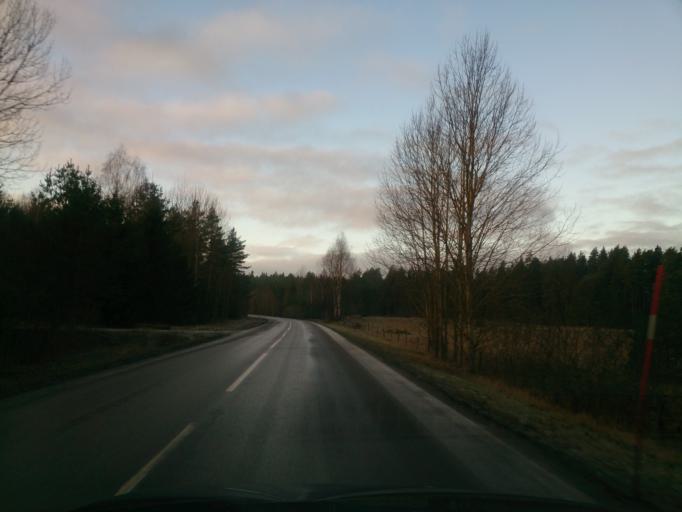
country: SE
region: OEstergoetland
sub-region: Linkopings Kommun
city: Linghem
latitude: 58.4053
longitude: 15.8316
